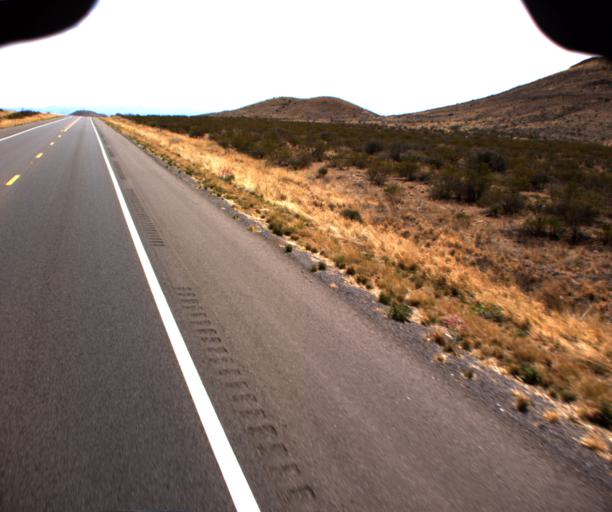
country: US
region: Arizona
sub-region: Cochise County
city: Willcox
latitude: 31.9055
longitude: -109.7562
